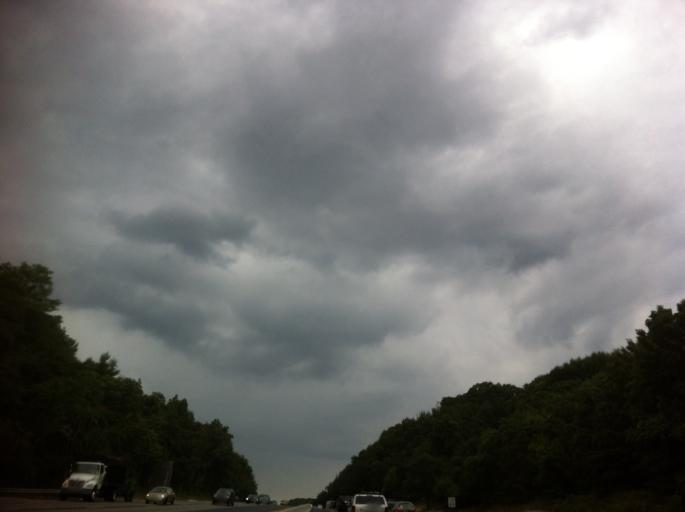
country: US
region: New Jersey
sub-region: Morris County
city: Mountain Lakes
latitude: 40.8830
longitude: -74.4696
